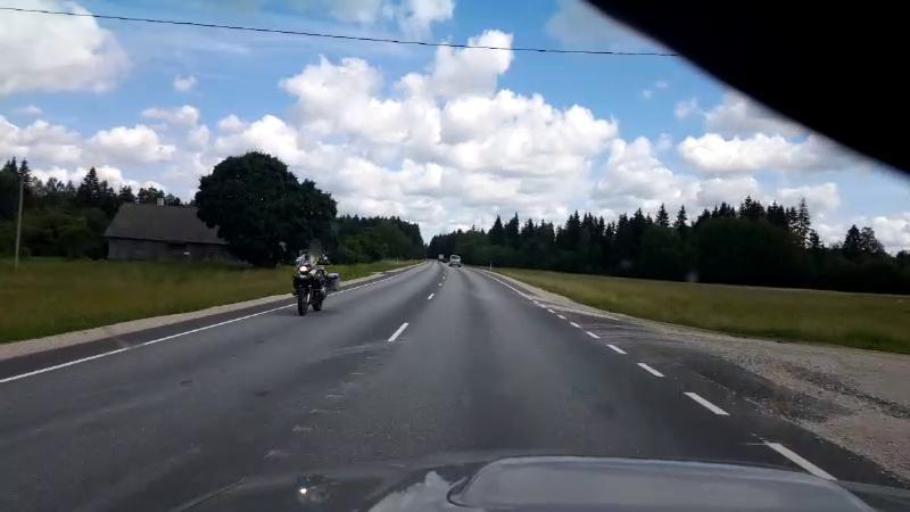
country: EE
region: Laeaene-Virumaa
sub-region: Tapa vald
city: Tapa
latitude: 59.2706
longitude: 26.0343
